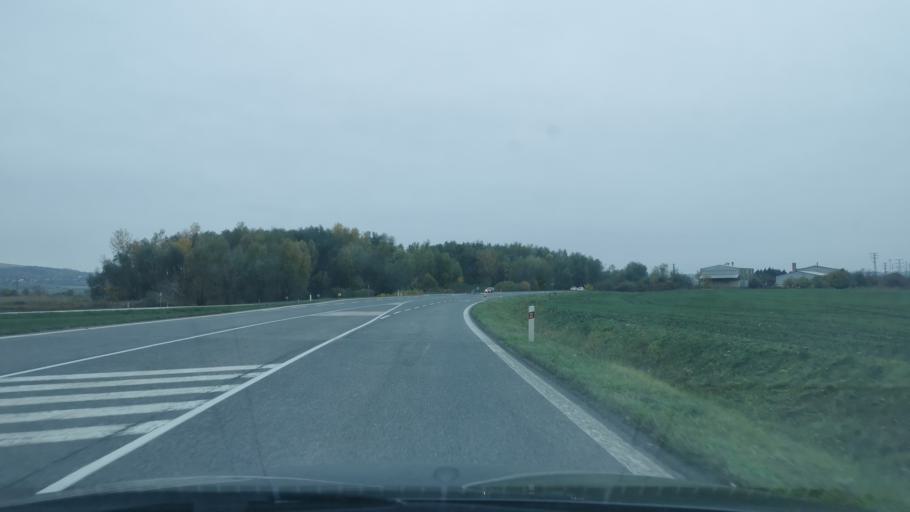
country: SK
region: Trnavsky
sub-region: Okres Skalica
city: Skalica
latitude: 48.8374
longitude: 17.2083
